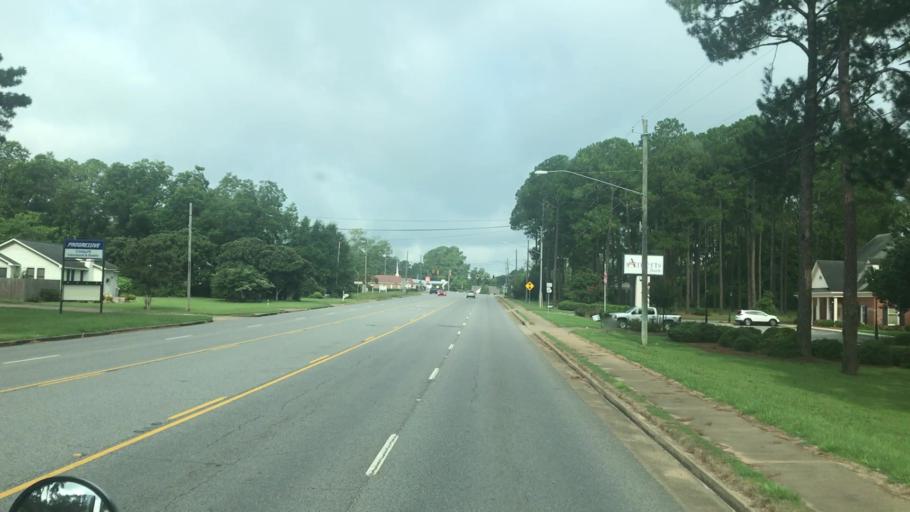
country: US
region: Georgia
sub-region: Miller County
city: Colquitt
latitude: 31.1699
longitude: -84.7304
